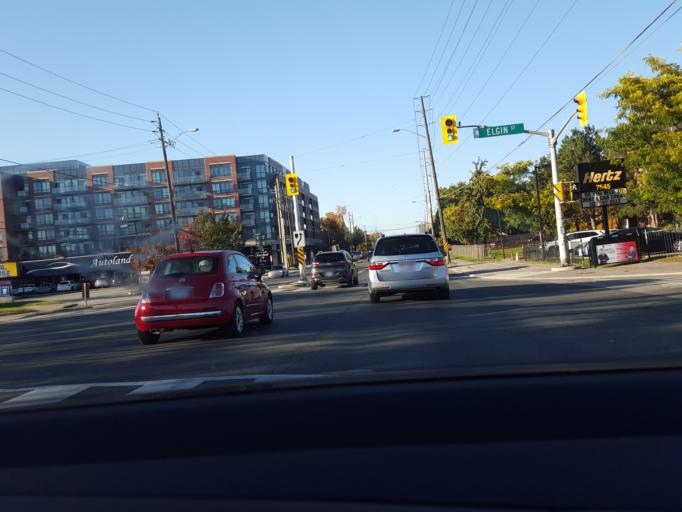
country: CA
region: Ontario
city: North York
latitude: 43.8113
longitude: -79.4233
